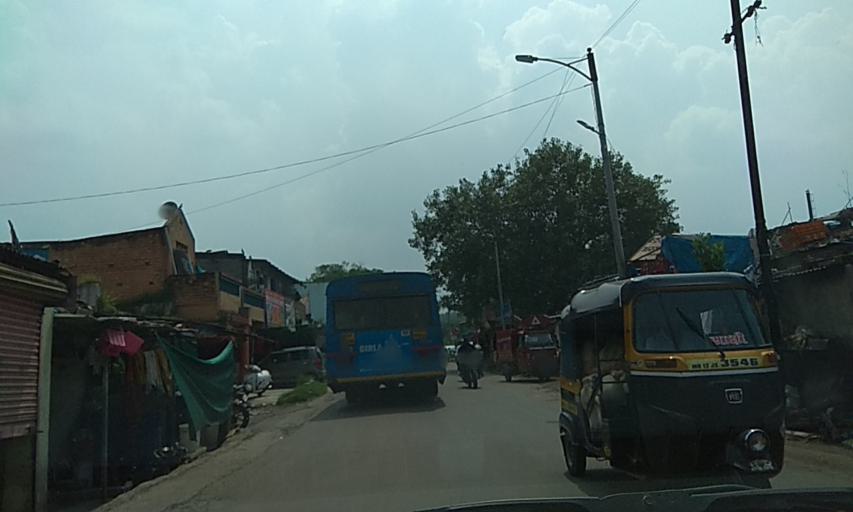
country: IN
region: Maharashtra
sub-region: Pune Division
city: Shivaji Nagar
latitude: 18.5394
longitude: 73.7939
